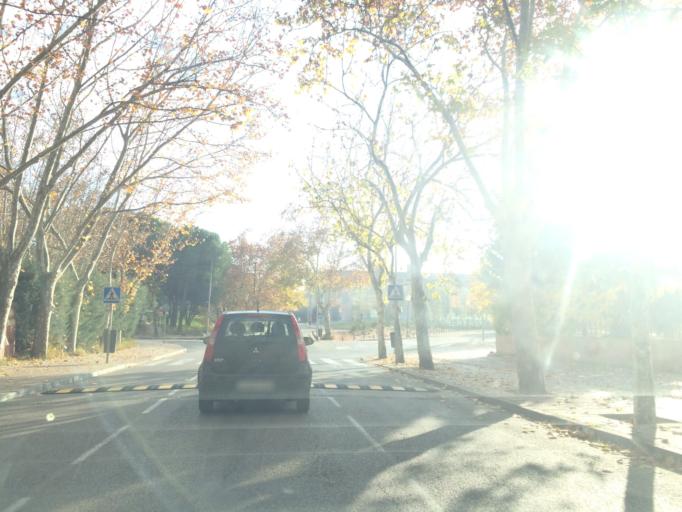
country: ES
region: Madrid
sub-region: Provincia de Madrid
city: Moncloa-Aravaca
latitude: 40.4473
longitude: -3.7246
